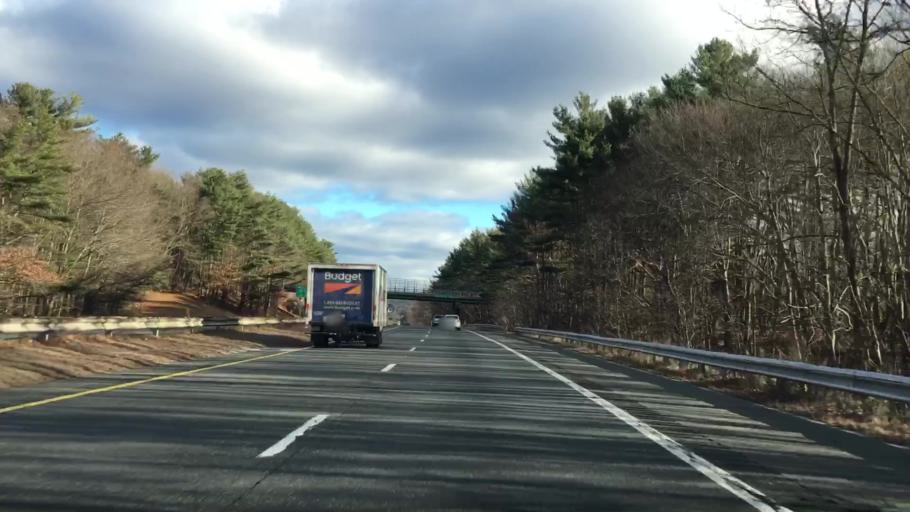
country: US
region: Massachusetts
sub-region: Hampden County
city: Three Rivers
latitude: 42.1585
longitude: -72.3653
